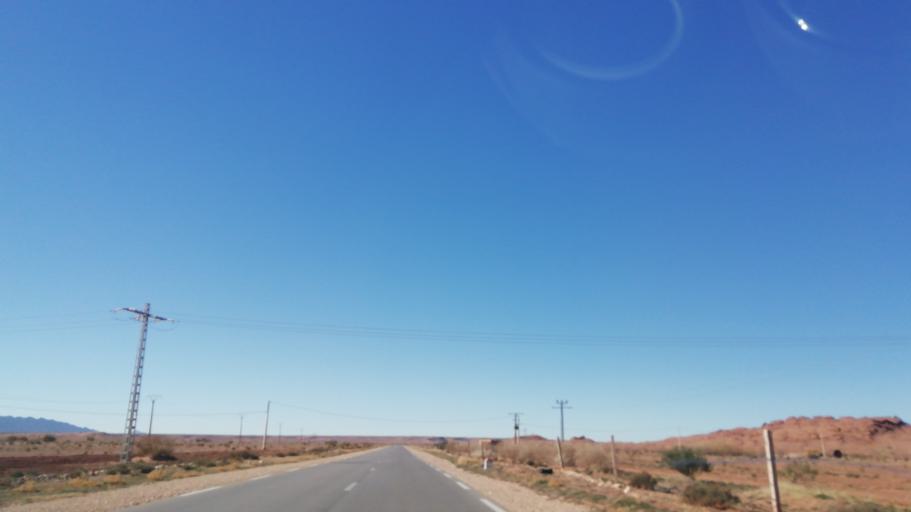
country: DZ
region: El Bayadh
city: El Abiodh Sidi Cheikh
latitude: 33.1755
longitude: 0.5282
